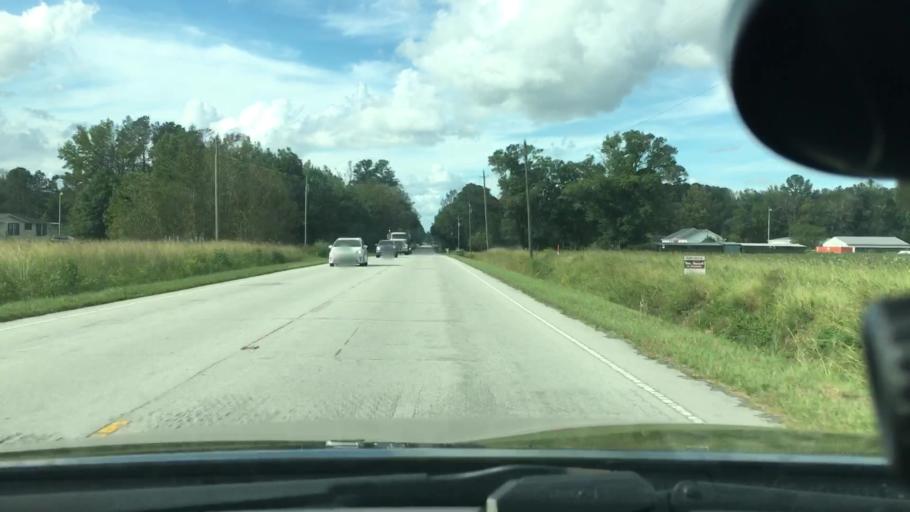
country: US
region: North Carolina
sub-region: Craven County
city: Vanceboro
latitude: 35.3878
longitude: -77.2285
